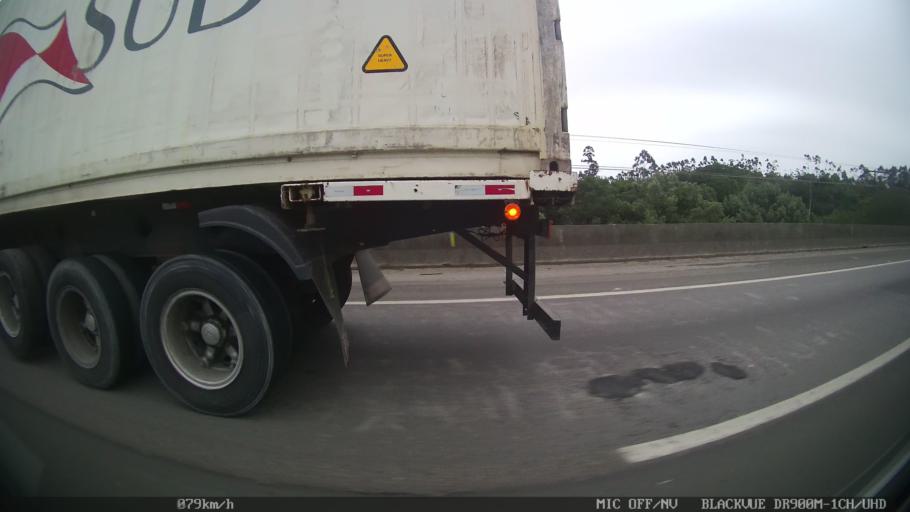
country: BR
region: Santa Catarina
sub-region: Penha
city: Penha
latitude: -26.7325
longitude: -48.7010
